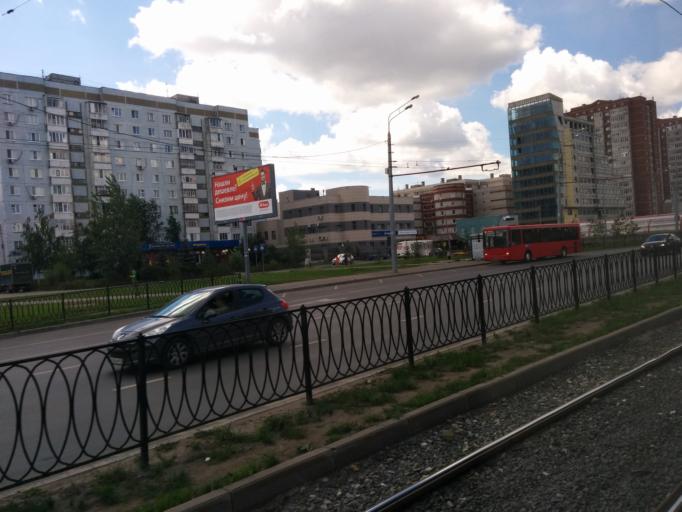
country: RU
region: Tatarstan
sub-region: Gorod Kazan'
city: Kazan
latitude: 55.8270
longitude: 49.1229
